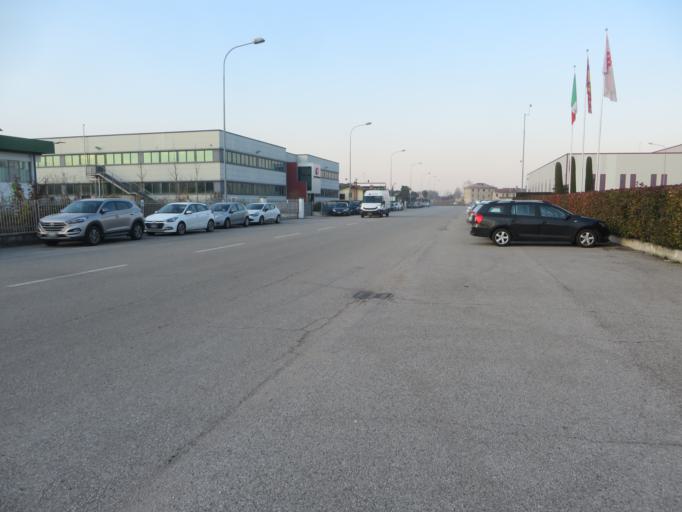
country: IT
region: Veneto
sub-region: Provincia di Verona
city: San Pietro di Morubio
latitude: 45.2296
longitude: 11.2433
